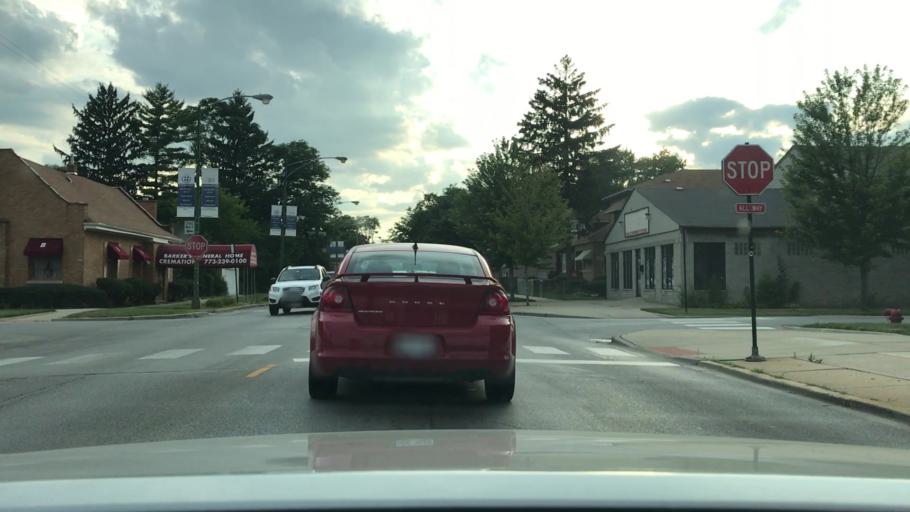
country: US
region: Illinois
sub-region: Cook County
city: Evergreen Park
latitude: 41.7141
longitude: -87.6549
